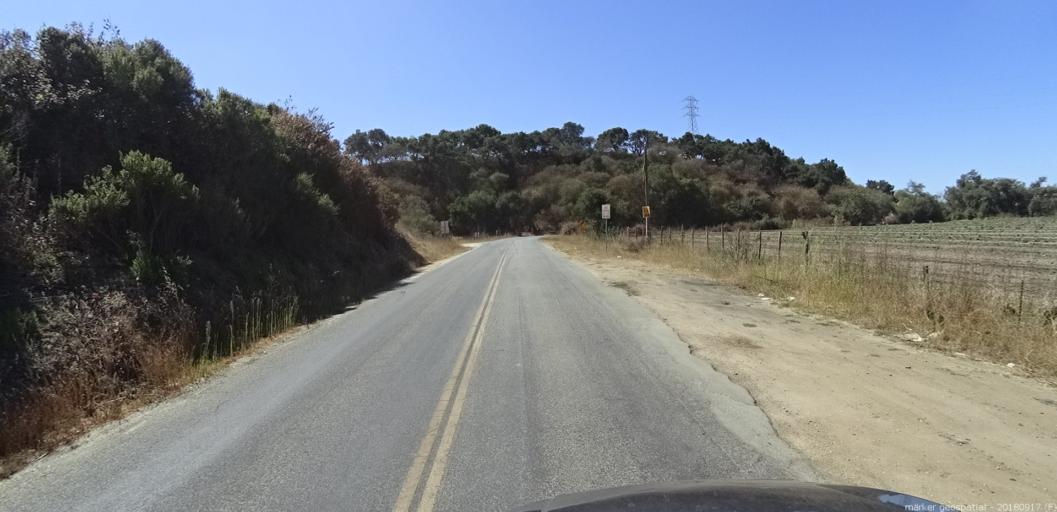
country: US
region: California
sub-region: Monterey County
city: Prunedale
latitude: 36.7587
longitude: -121.6028
